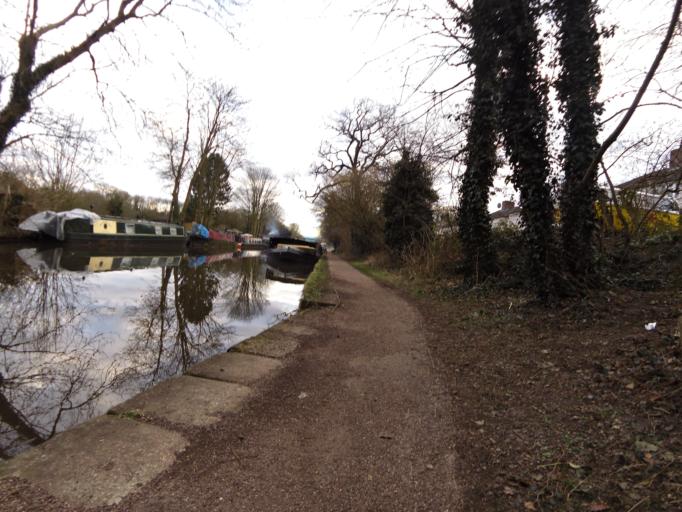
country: GB
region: England
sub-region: Hertfordshire
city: Watford
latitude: 51.6562
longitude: -0.4277
